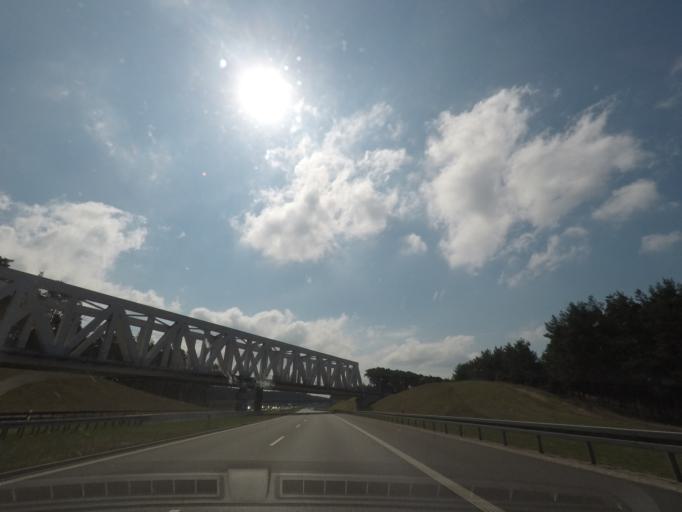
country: PL
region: Kujawsko-Pomorskie
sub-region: Powiat aleksandrowski
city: Aleksandrow Kujawski
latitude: 52.9404
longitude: 18.6956
